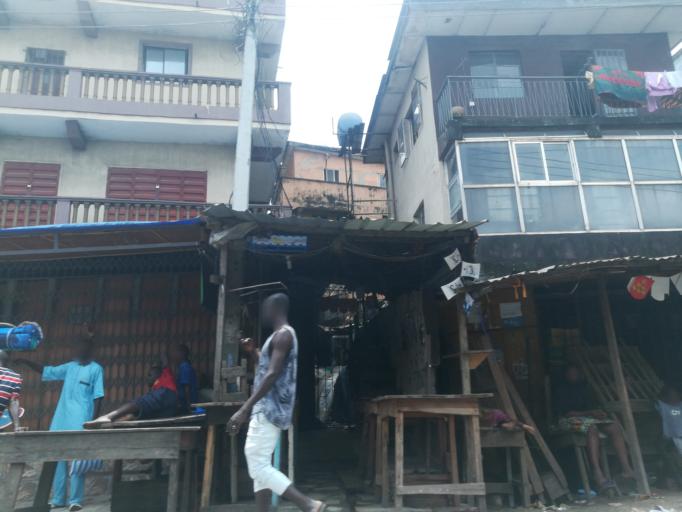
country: NG
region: Lagos
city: Lagos
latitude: 6.4617
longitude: 3.3842
